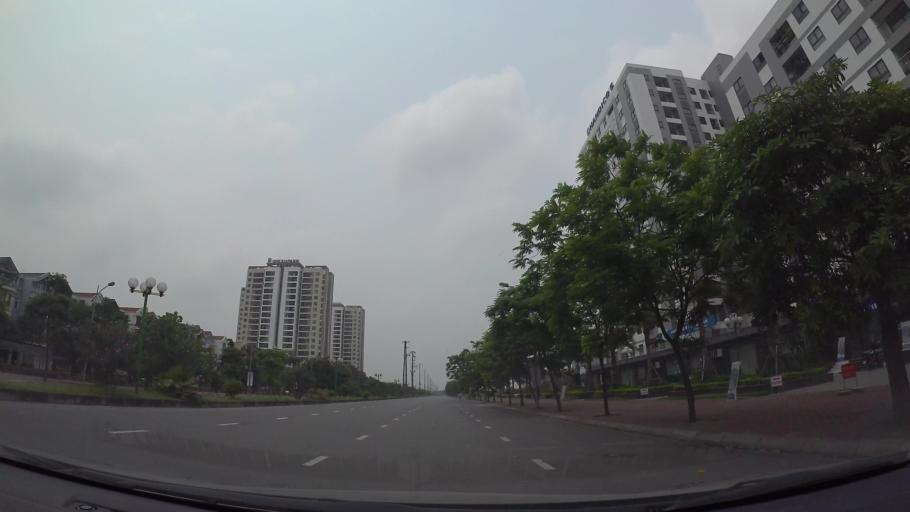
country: VN
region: Ha Noi
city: Trau Quy
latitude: 21.0621
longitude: 105.9130
